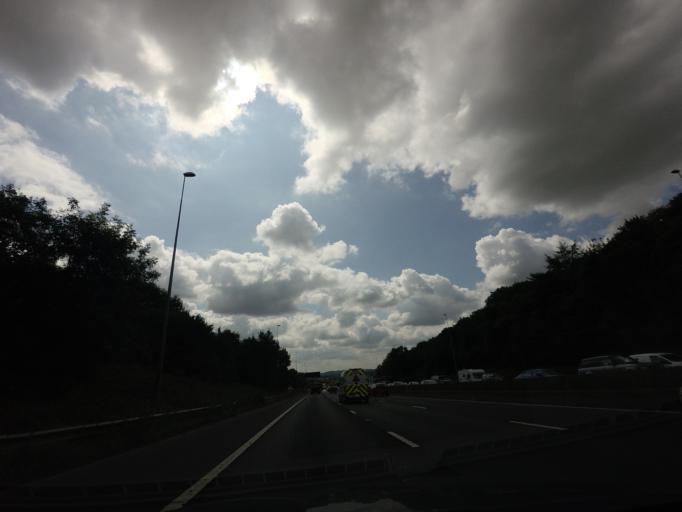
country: GB
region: England
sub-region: Borough of Wigan
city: Shevington
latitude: 53.5814
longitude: -2.6938
